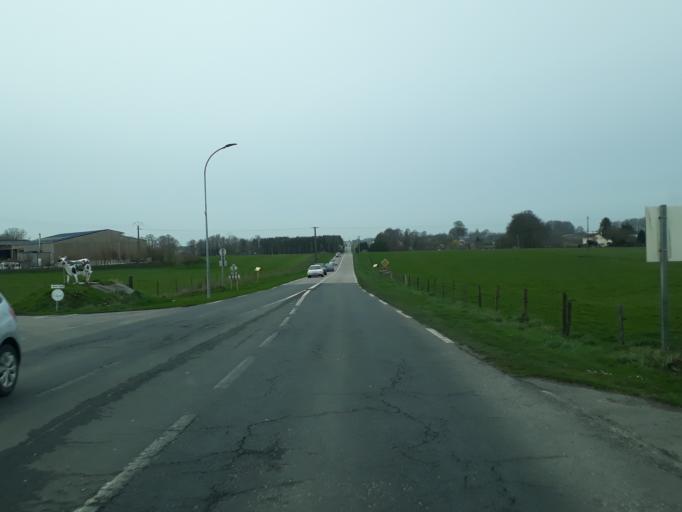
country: FR
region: Haute-Normandie
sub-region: Departement de la Seine-Maritime
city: Breaute
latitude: 49.6295
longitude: 0.3945
